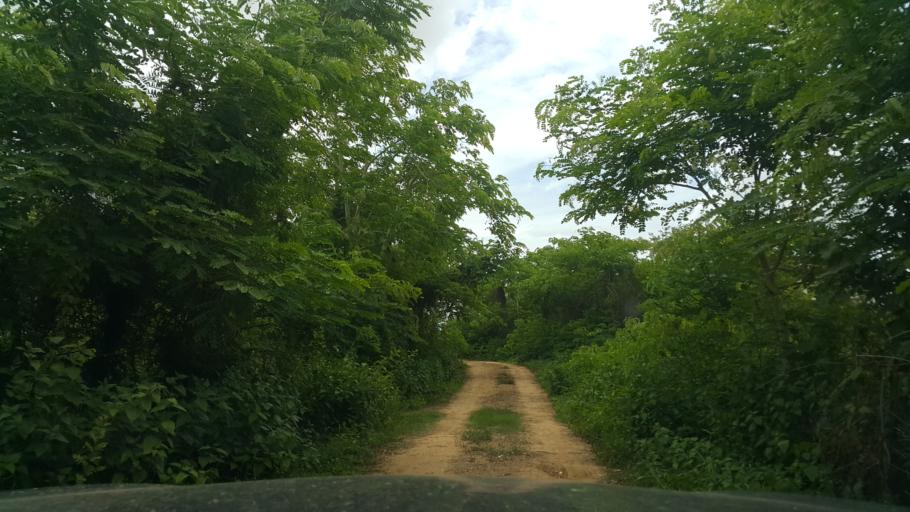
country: TH
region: Sukhothai
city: Sukhothai
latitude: 17.0343
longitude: 99.7973
